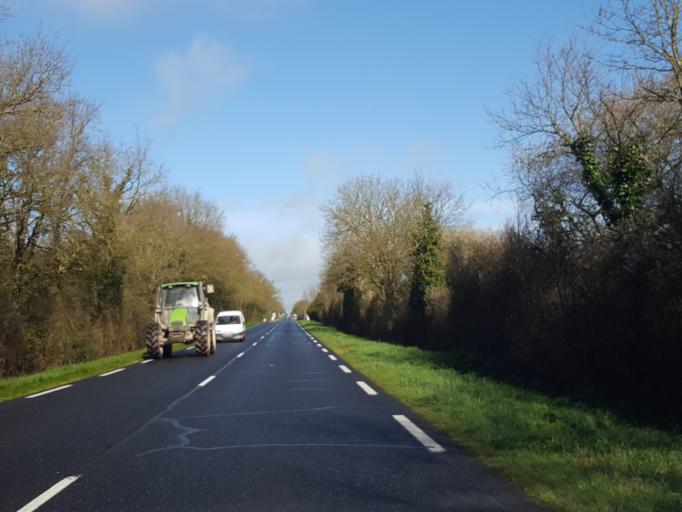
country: FR
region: Pays de la Loire
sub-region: Departement de la Vendee
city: Saligny
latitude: 46.7996
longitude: -1.4477
